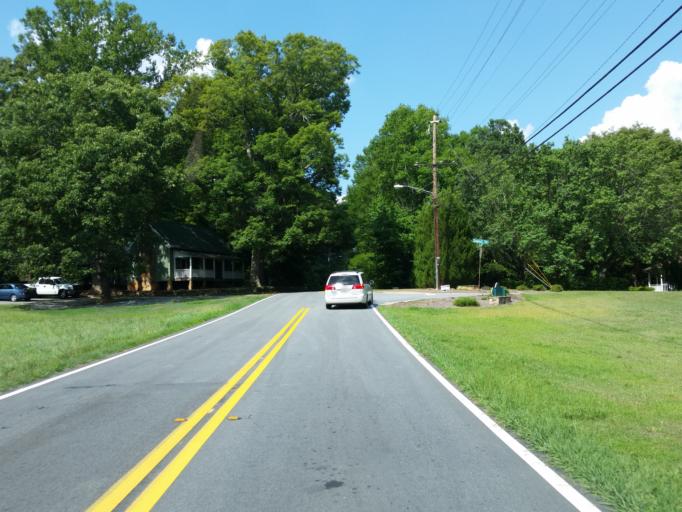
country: US
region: Georgia
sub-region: Fulton County
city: Roswell
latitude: 34.0324
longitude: -84.4495
